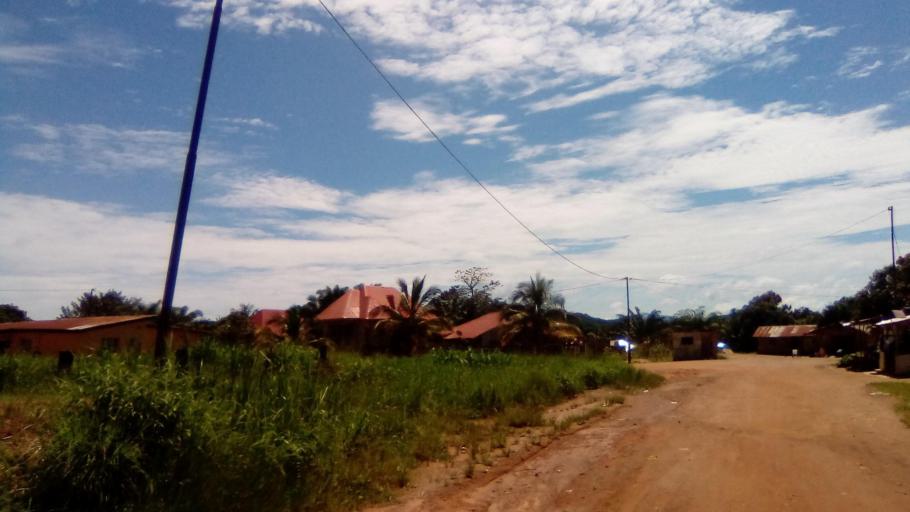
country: SL
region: Eastern Province
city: Simbakoro
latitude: 8.6290
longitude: -10.9942
